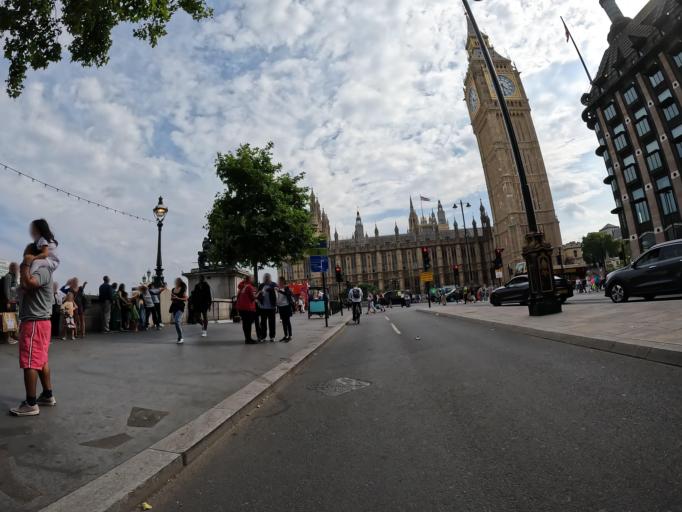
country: GB
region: England
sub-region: Greater London
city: Orpington
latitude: 51.3433
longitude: 0.0990
